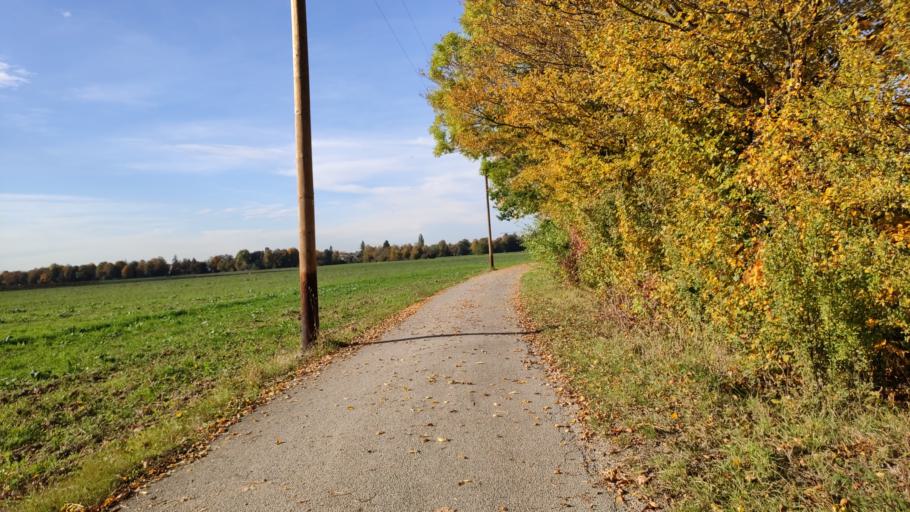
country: DE
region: Bavaria
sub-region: Upper Bavaria
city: Pasing
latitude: 48.1335
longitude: 11.4739
